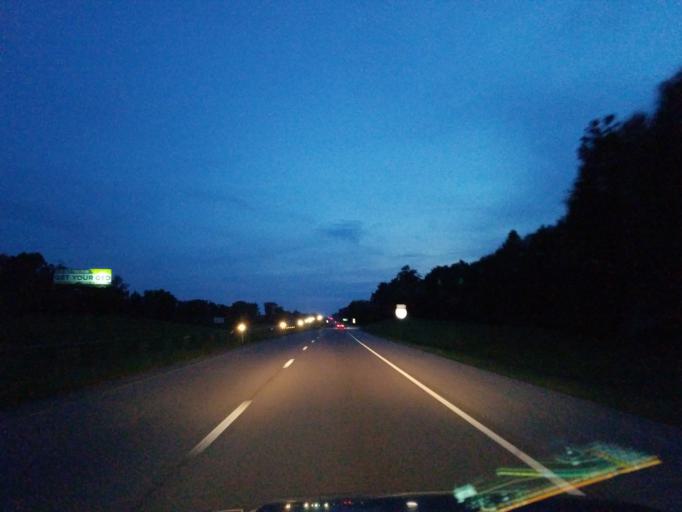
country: US
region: Mississippi
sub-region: Jones County
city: Ellisville
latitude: 31.5821
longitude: -89.2415
